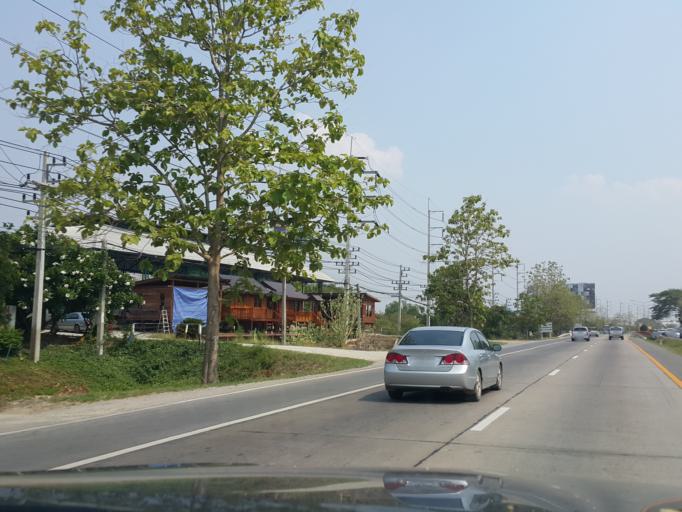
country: TH
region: Lamphun
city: Ban Thi
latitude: 18.6488
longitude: 99.0532
